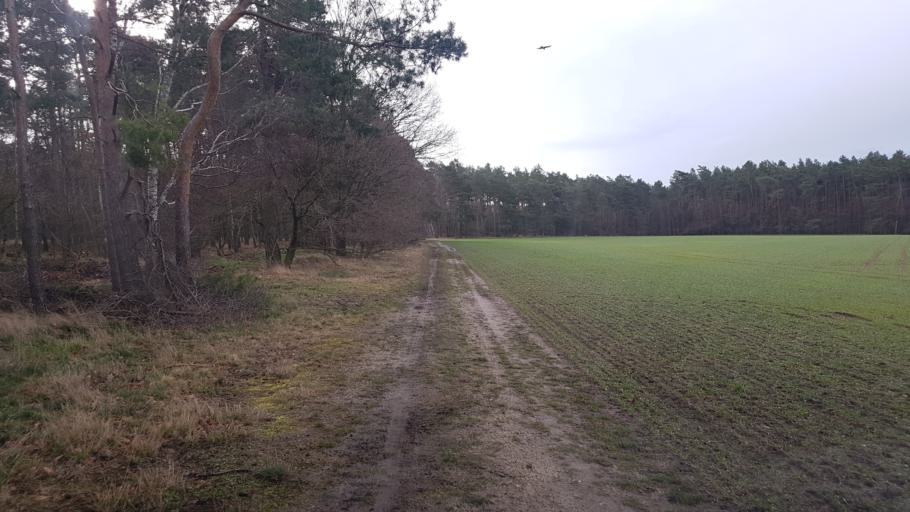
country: DE
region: Brandenburg
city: Sallgast
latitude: 51.6109
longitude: 13.8158
